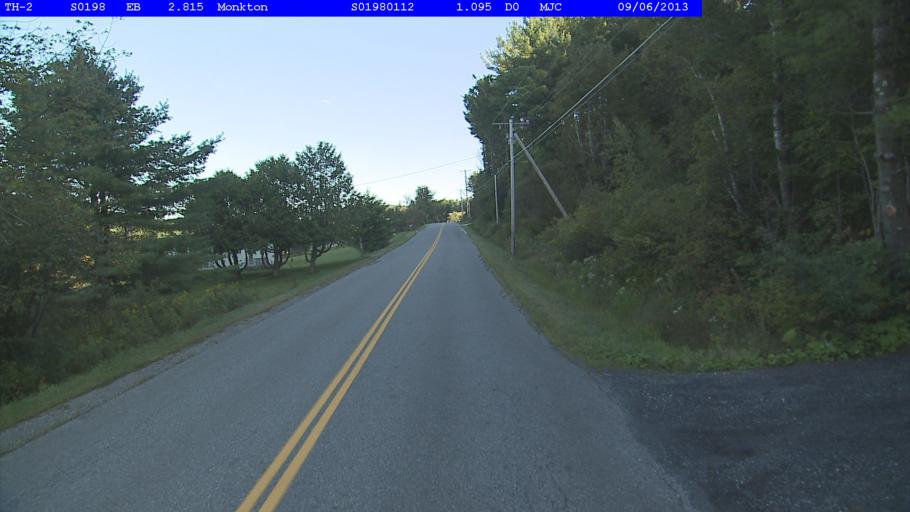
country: US
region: Vermont
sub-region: Chittenden County
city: Hinesburg
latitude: 44.2502
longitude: -73.1761
